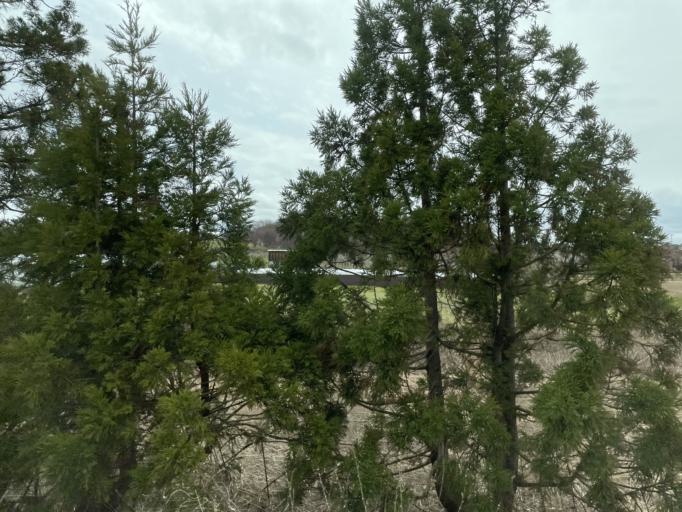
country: JP
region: Aomori
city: Shimokizukuri
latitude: 40.7871
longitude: 140.3000
